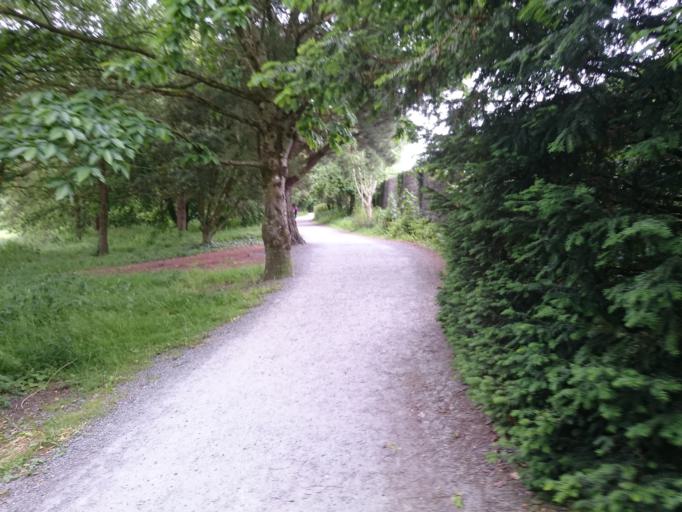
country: IE
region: Leinster
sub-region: Kilkenny
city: Kilkenny
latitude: 52.6478
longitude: -7.2421
